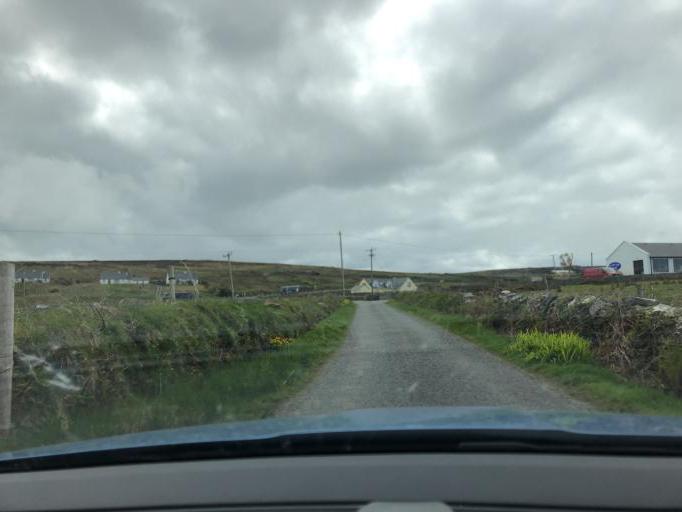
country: IE
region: Munster
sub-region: An Clar
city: Kilrush
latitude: 52.9924
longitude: -9.4058
